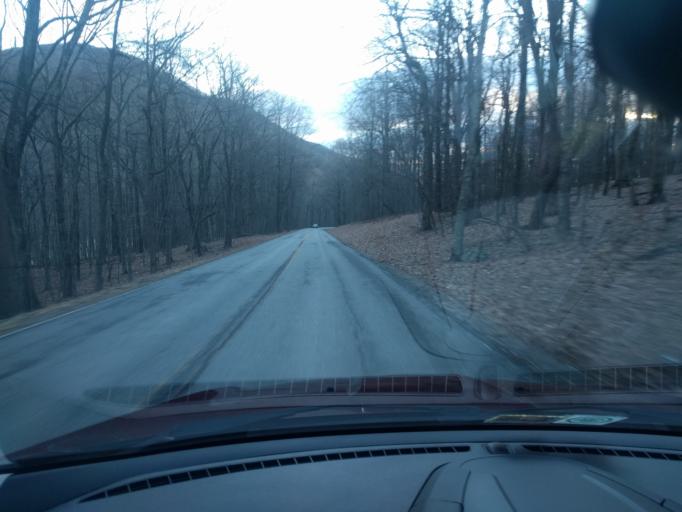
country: US
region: Virginia
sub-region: Botetourt County
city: Buchanan
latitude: 37.4436
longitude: -79.6046
